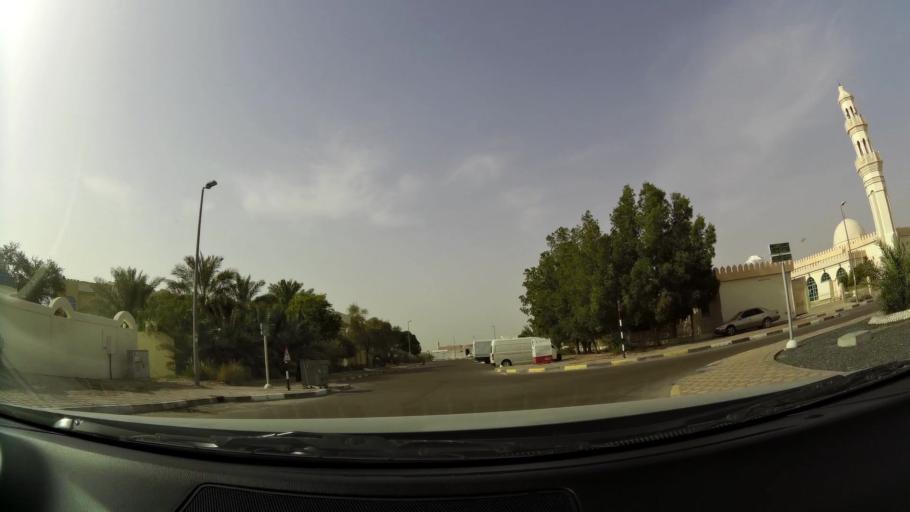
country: AE
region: Abu Dhabi
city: Al Ain
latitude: 24.1462
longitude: 55.7111
